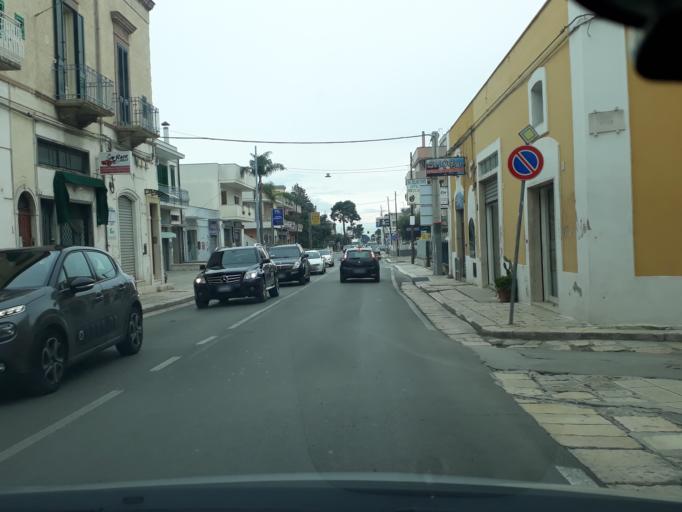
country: IT
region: Apulia
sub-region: Provincia di Brindisi
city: Fasano
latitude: 40.8347
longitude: 17.3638
